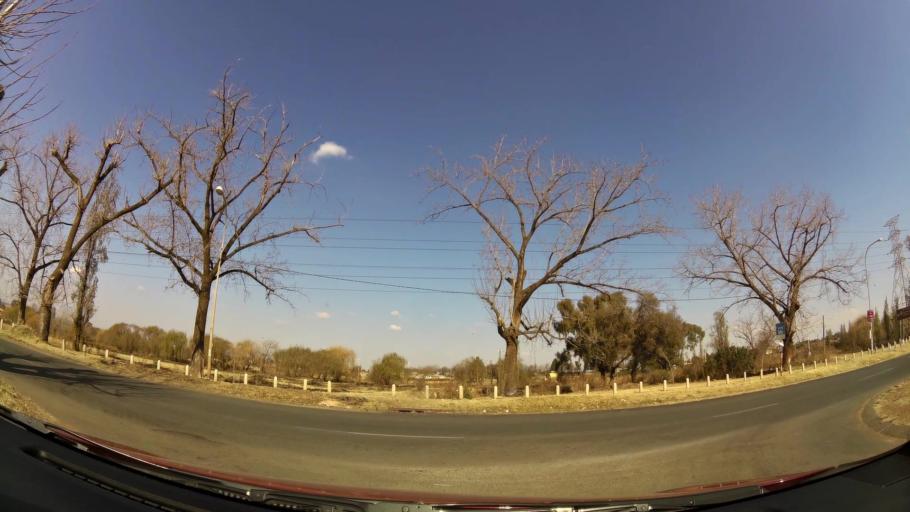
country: ZA
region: Gauteng
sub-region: City of Johannesburg Metropolitan Municipality
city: Soweto
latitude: -26.2387
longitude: 27.8796
